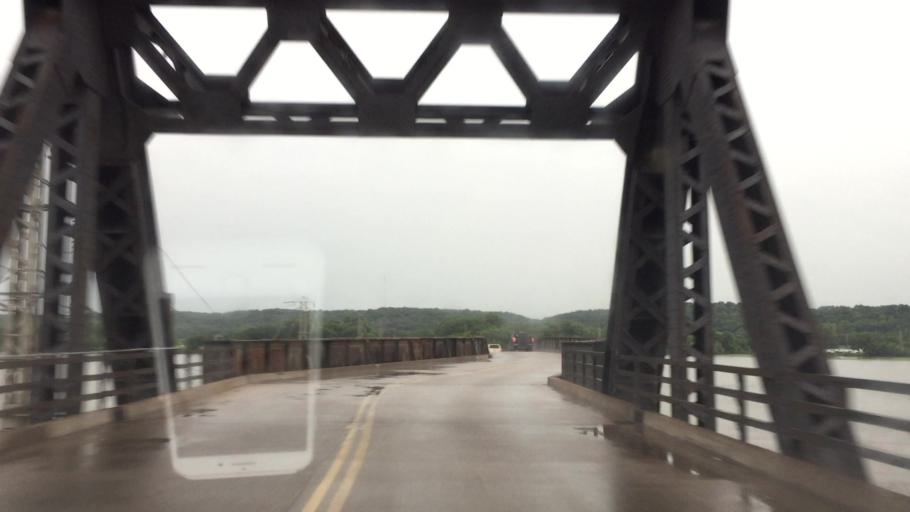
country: US
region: Iowa
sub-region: Lee County
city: Fort Madison
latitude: 40.6252
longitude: -91.2940
